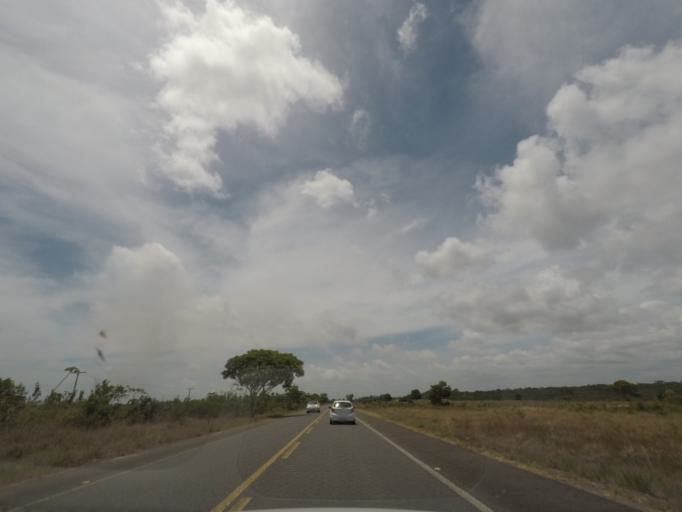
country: BR
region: Bahia
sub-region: Conde
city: Conde
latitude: -11.7432
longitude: -37.5811
